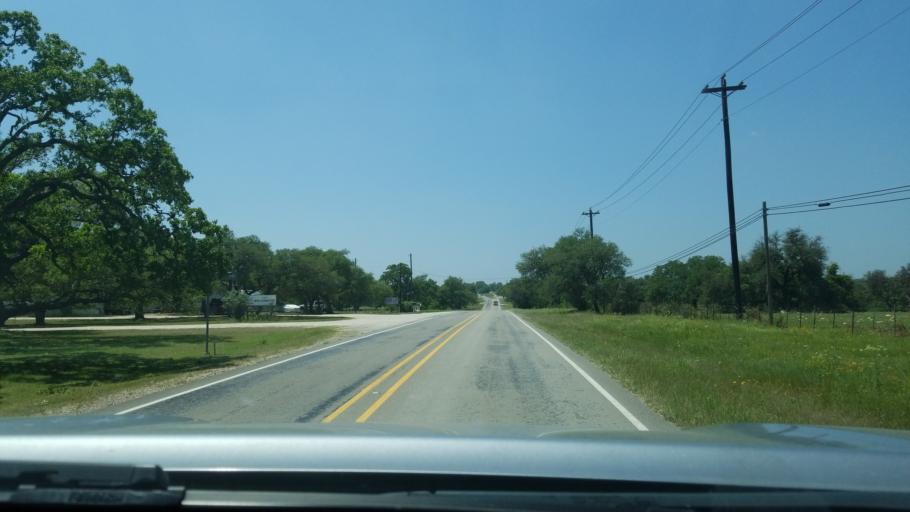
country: US
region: Texas
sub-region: Blanco County
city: Blanco
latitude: 30.0684
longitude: -98.4017
